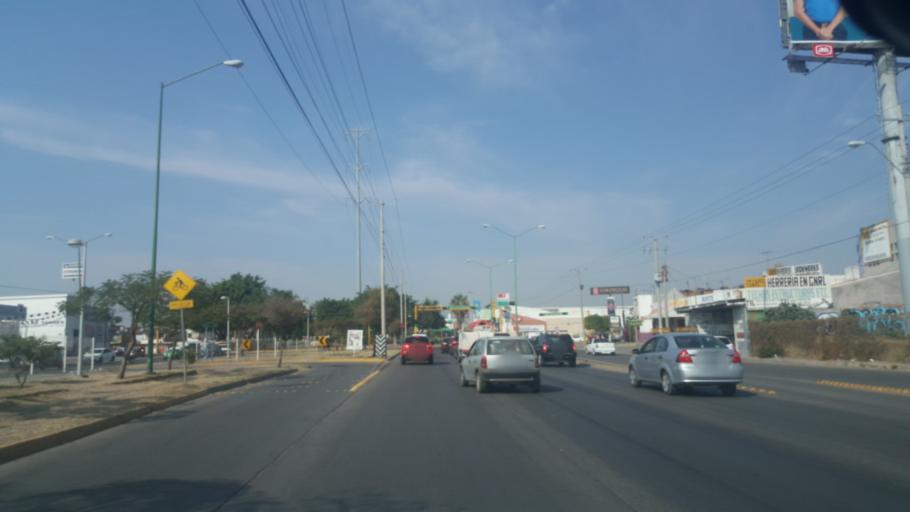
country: MX
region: Guanajuato
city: Leon
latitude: 21.1461
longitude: -101.6501
